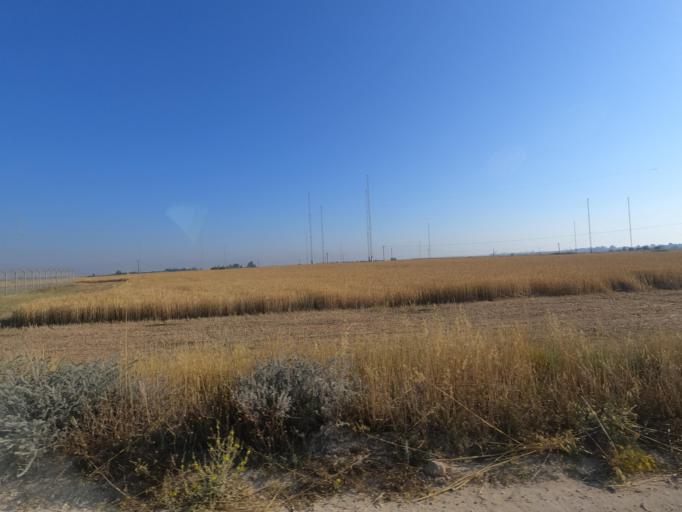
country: CY
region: Ammochostos
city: Acheritou
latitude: 35.0939
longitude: 33.8921
